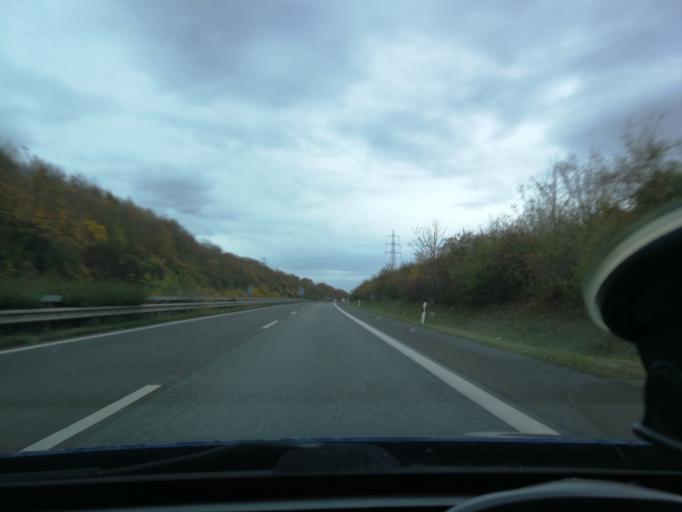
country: DE
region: Rheinland-Pfalz
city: Trierweiler
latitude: 49.7486
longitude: 6.5623
